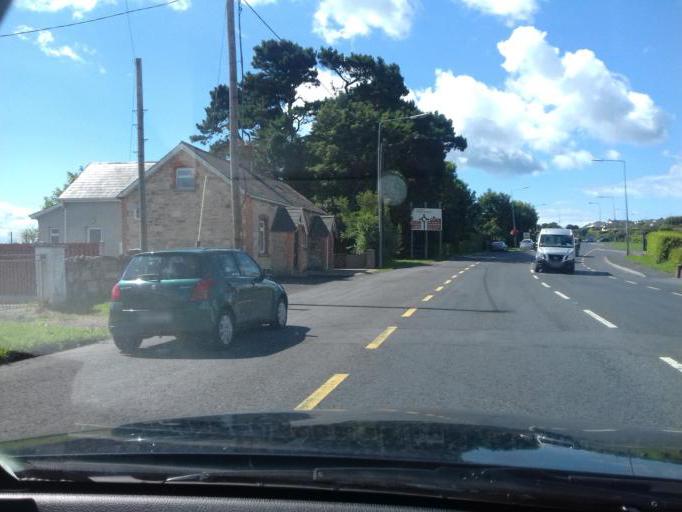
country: IE
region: Munster
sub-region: Waterford
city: Tra Mhor
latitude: 52.1704
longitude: -7.1419
